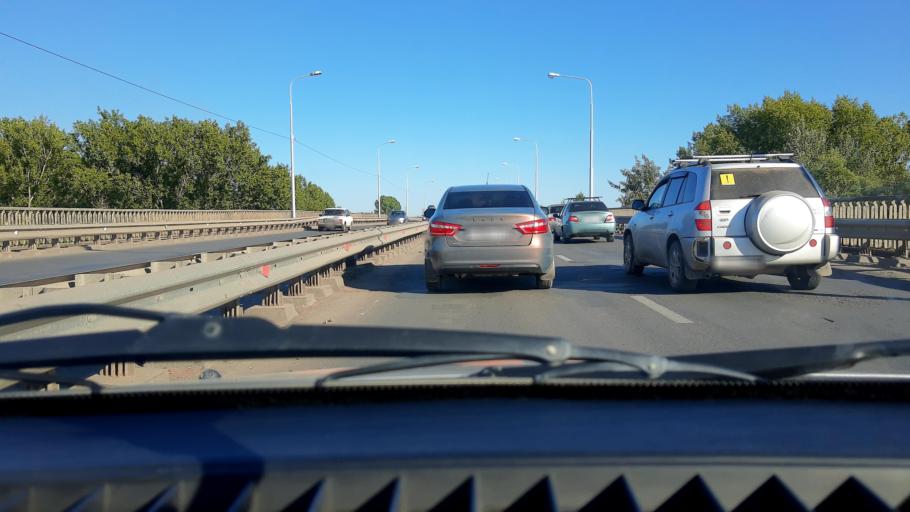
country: RU
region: Bashkortostan
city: Iglino
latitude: 54.7703
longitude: 56.2057
